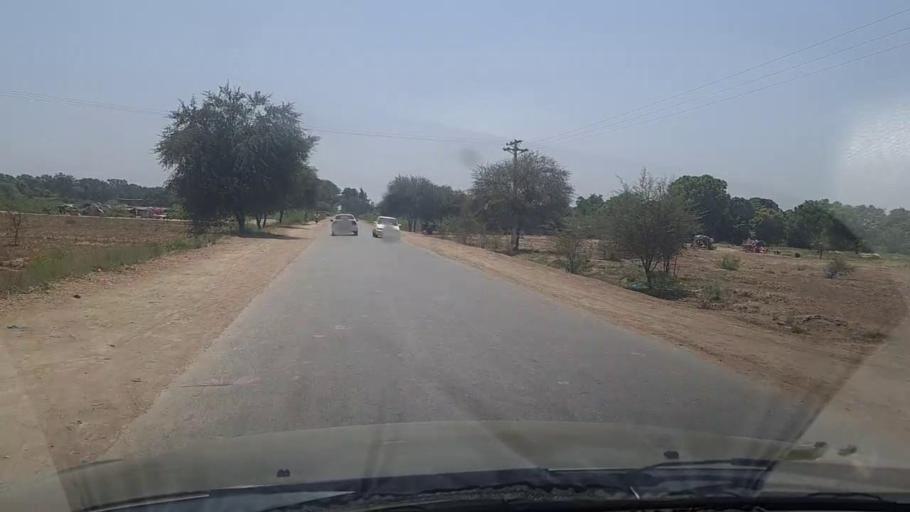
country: PK
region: Sindh
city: Tando Jam
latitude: 25.3056
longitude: 68.5793
